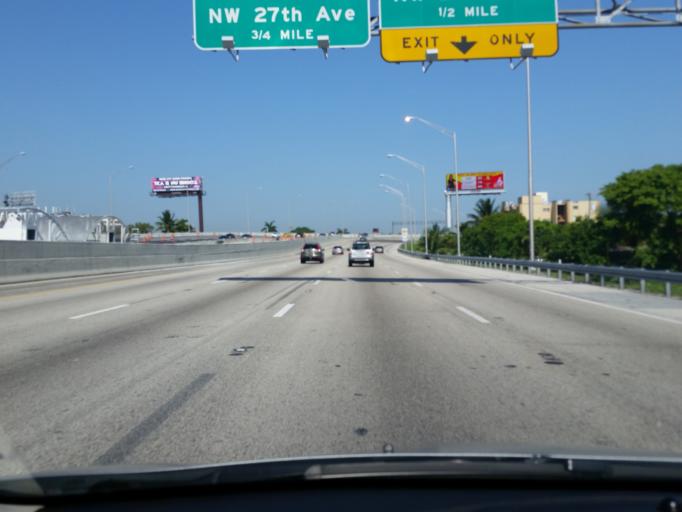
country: US
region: Florida
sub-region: Miami-Dade County
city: Allapattah
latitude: 25.7826
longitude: -80.2285
